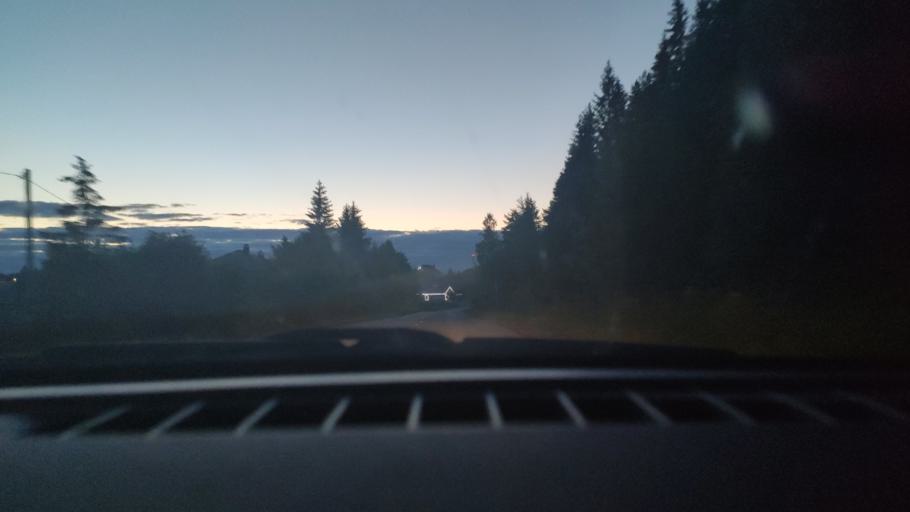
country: RU
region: Perm
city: Polazna
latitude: 58.2770
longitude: 56.4079
